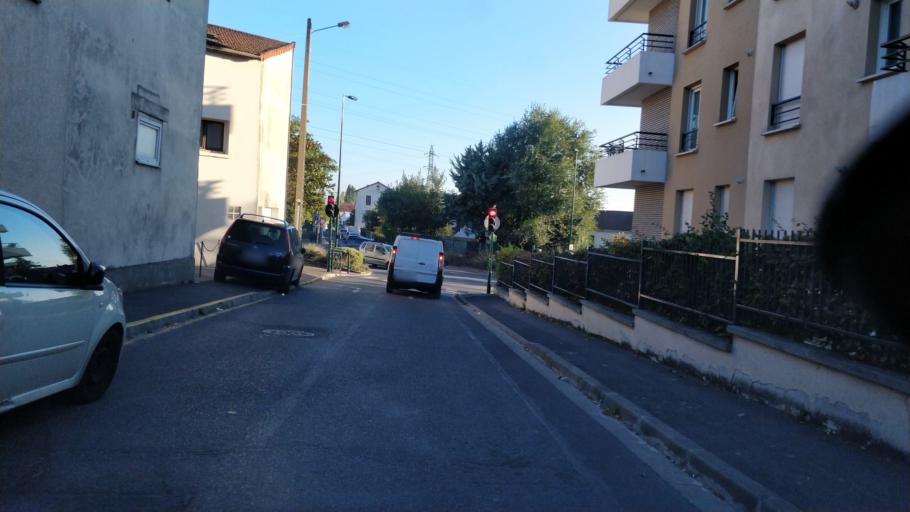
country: FR
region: Ile-de-France
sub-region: Departement de Seine-Saint-Denis
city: Gagny
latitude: 48.8822
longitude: 2.5391
